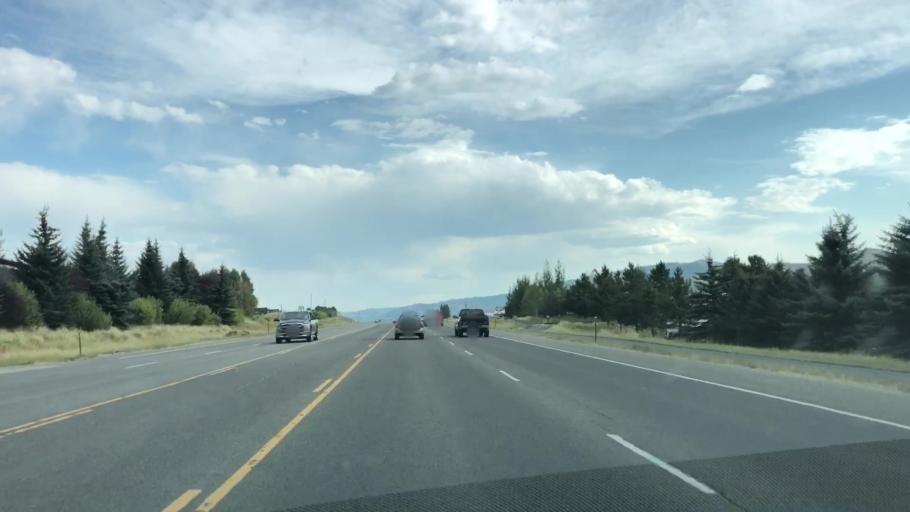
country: US
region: Wyoming
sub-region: Teton County
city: South Park
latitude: 43.4232
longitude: -110.7769
